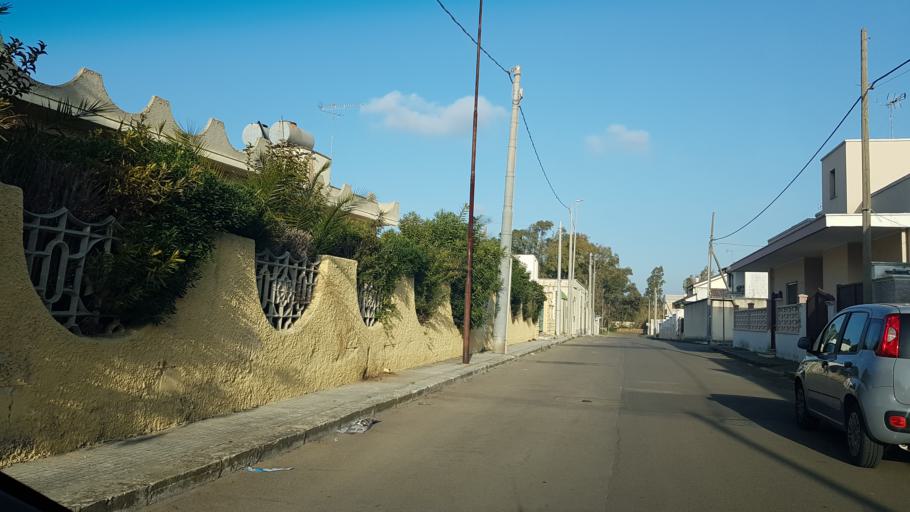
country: IT
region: Apulia
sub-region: Provincia di Lecce
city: Trepuzzi
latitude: 40.4117
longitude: 18.0706
